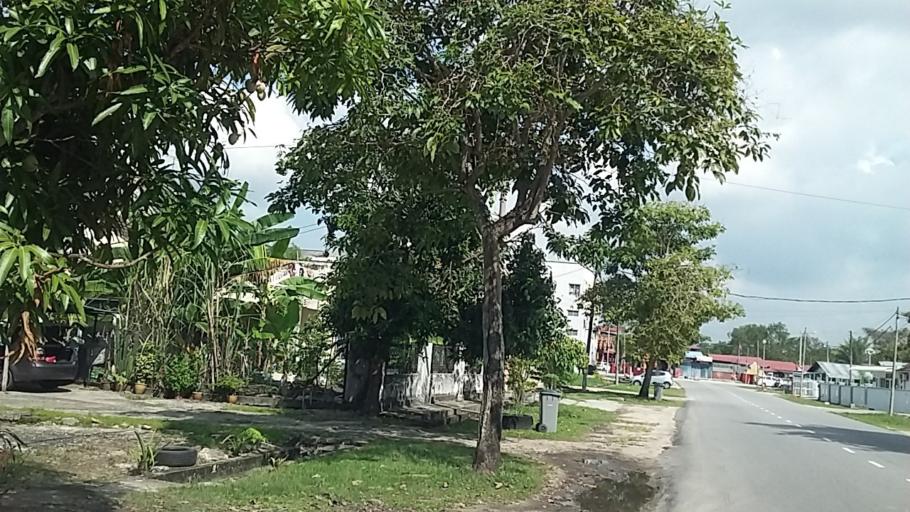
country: MY
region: Johor
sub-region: Daerah Batu Pahat
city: Batu Pahat
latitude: 1.8428
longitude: 102.9256
